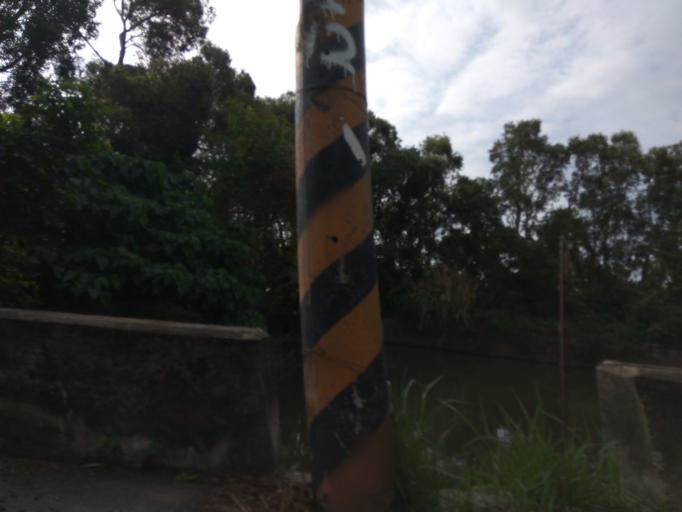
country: TW
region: Taiwan
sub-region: Hsinchu
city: Zhubei
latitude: 24.9810
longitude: 121.0311
